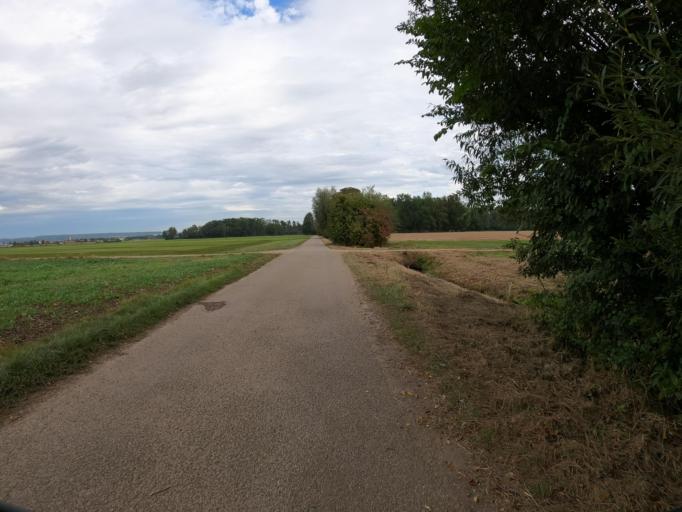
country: DE
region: Bavaria
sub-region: Swabia
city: Holzheim
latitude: 48.3949
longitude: 10.0764
